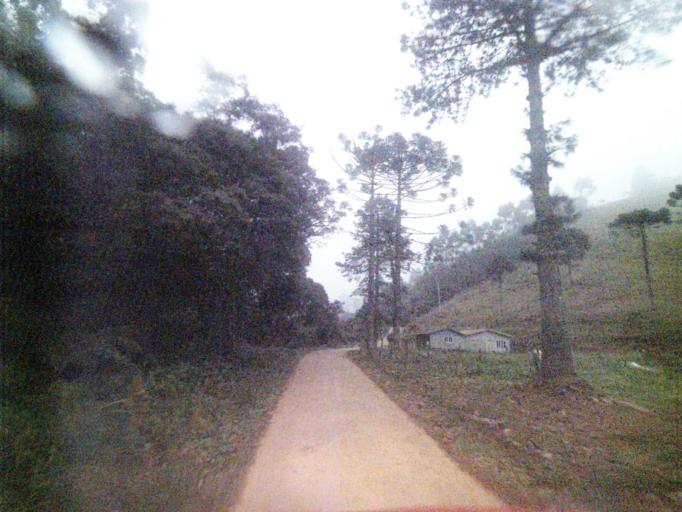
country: BR
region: Santa Catarina
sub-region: Anitapolis
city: Anitapolis
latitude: -27.7989
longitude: -49.1393
